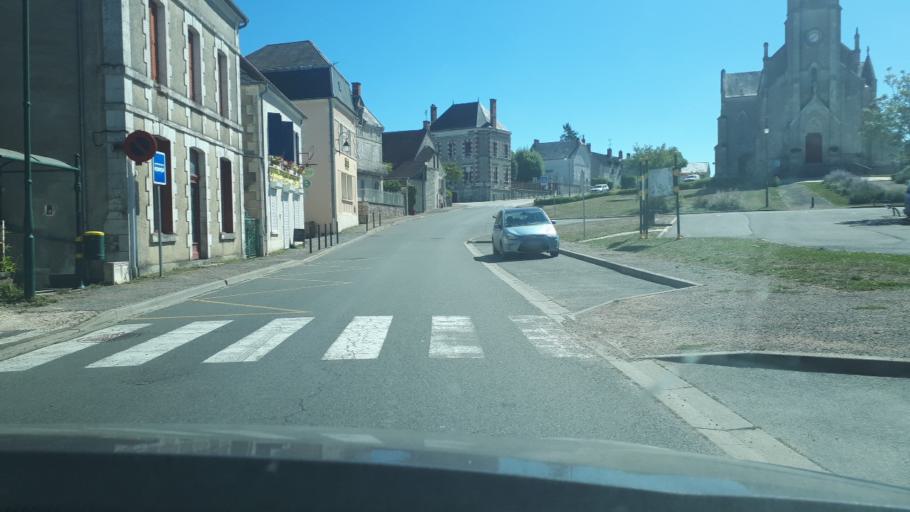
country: FR
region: Centre
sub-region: Departement du Cher
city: Sancerre
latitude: 47.2579
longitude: 2.7572
